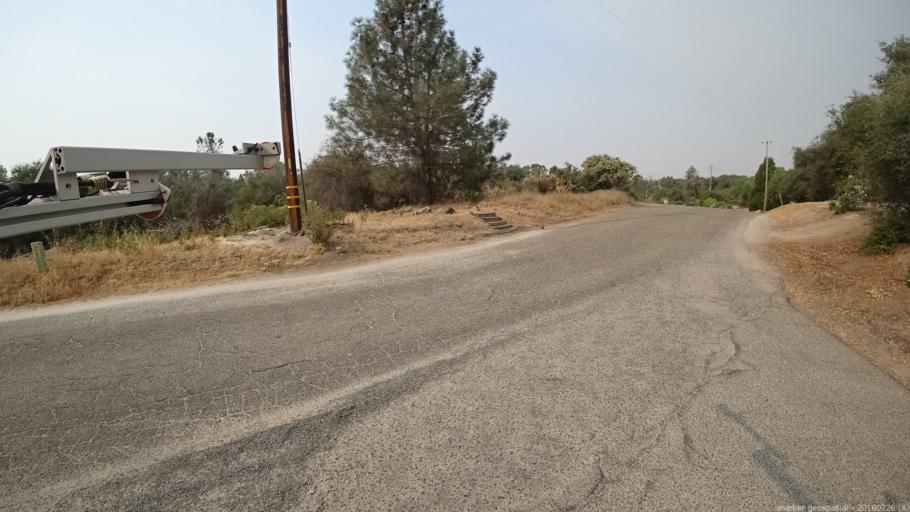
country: US
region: California
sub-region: Madera County
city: Coarsegold
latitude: 37.2160
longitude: -119.7000
